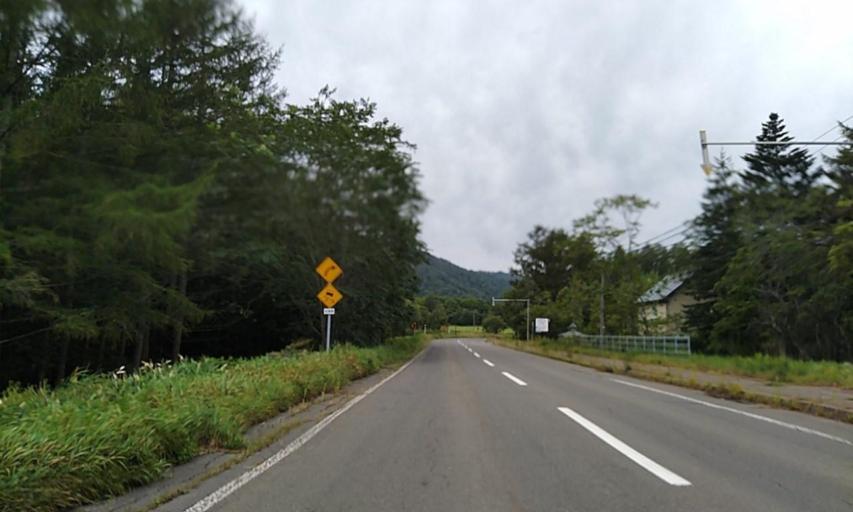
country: JP
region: Hokkaido
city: Bihoro
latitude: 43.5536
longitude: 144.3352
